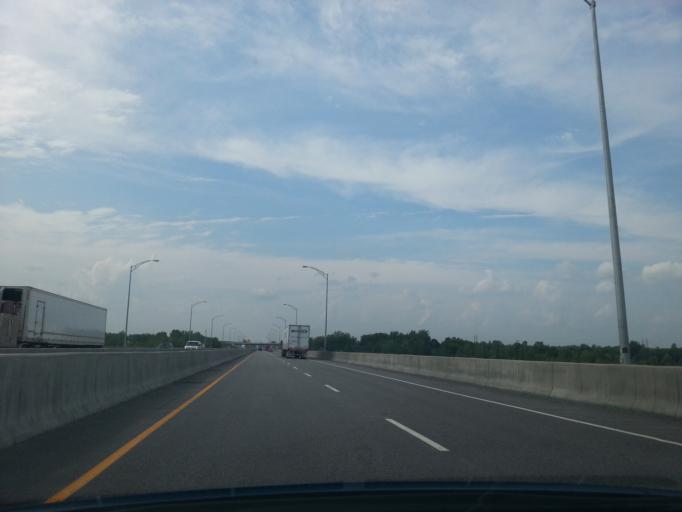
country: CA
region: Quebec
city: Les Cedres
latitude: 45.3073
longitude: -74.0151
